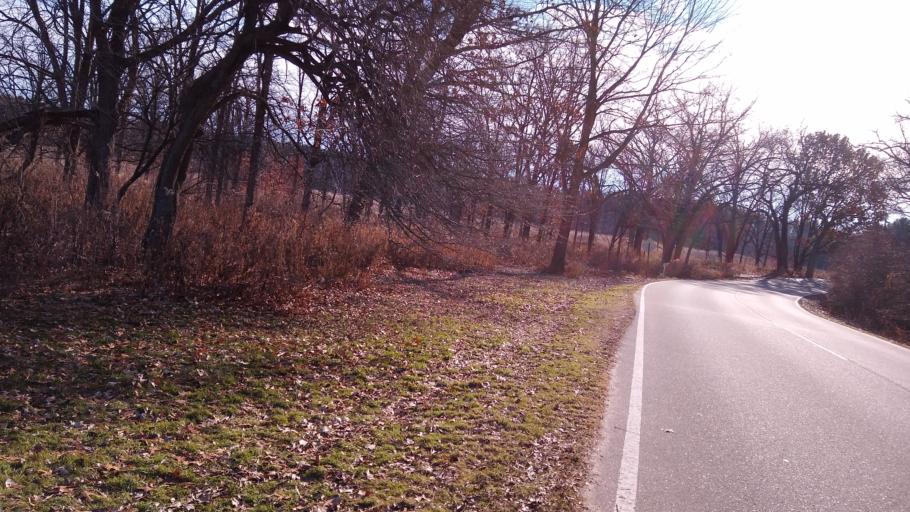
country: US
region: Wisconsin
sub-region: Dane County
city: Shorewood Hills
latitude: 43.0398
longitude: -89.4325
